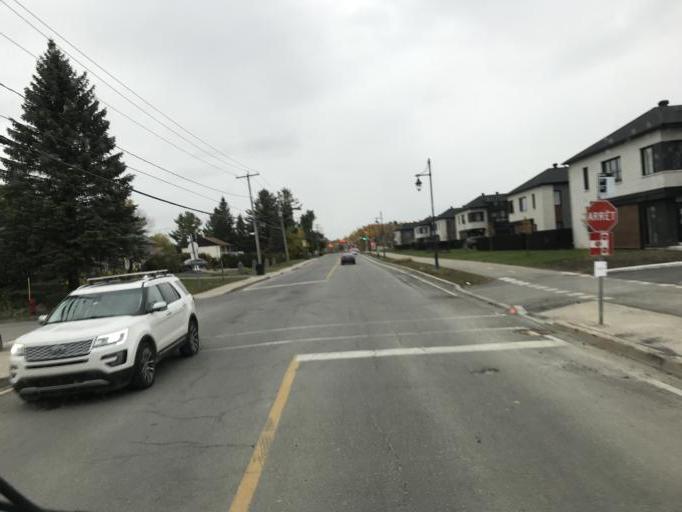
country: CA
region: Quebec
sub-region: Lanaudiere
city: Lorraine
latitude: 45.6875
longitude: -73.7845
